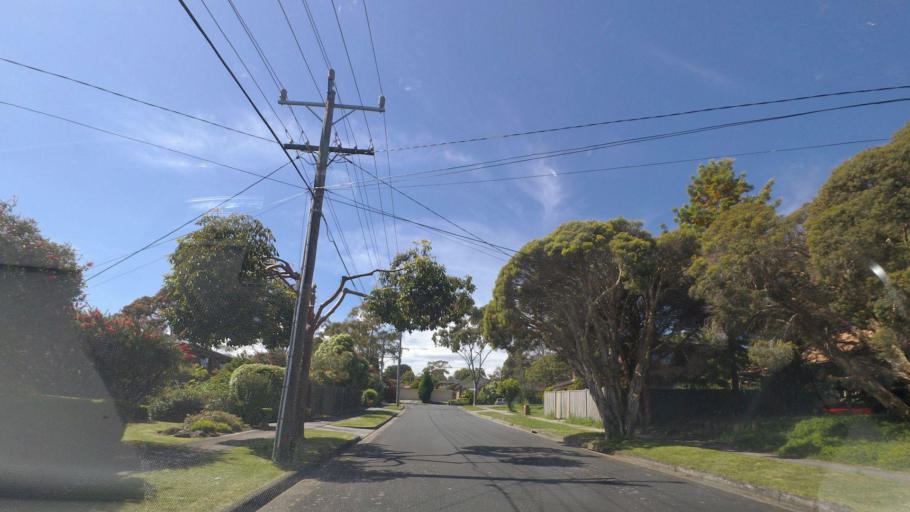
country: AU
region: Victoria
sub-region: Whitehorse
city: Vermont
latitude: -37.8511
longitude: 145.1979
